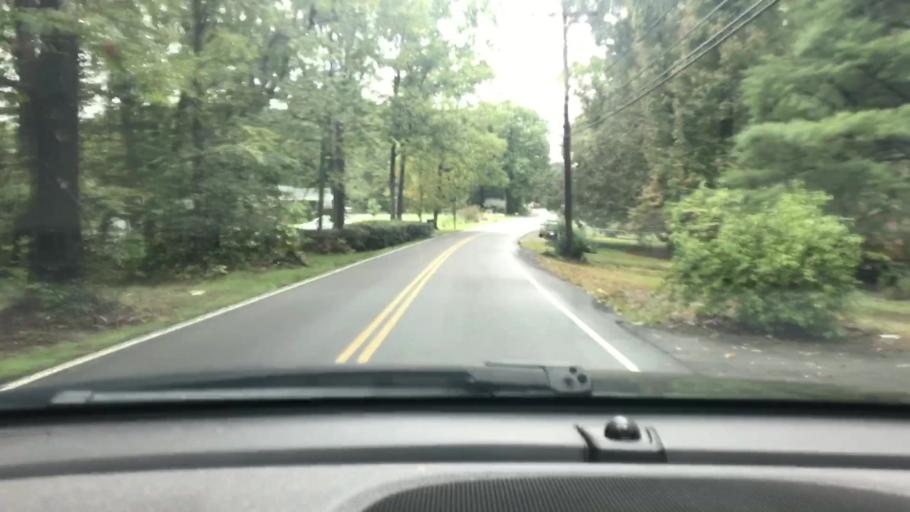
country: US
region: Tennessee
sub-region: Cheatham County
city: Kingston Springs
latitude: 36.1094
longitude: -87.1416
